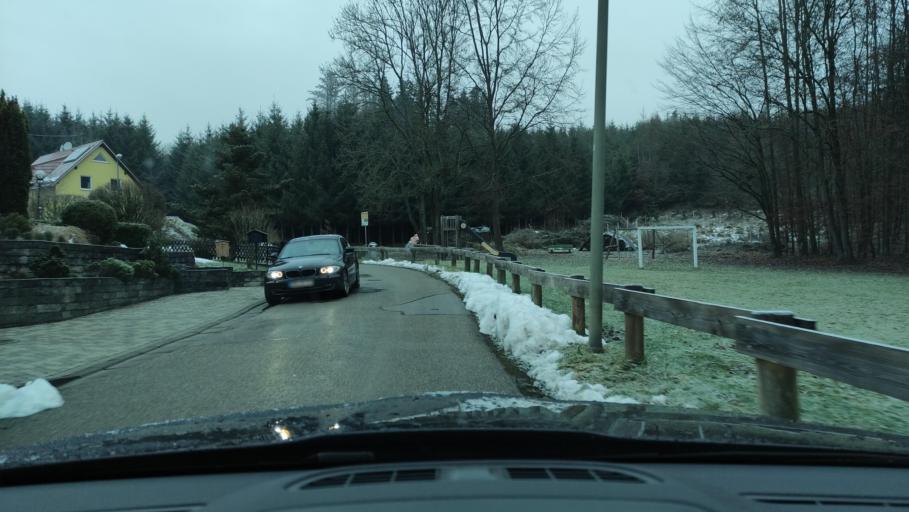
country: DE
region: Bavaria
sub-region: Swabia
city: Krumbach
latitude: 48.2536
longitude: 10.3503
